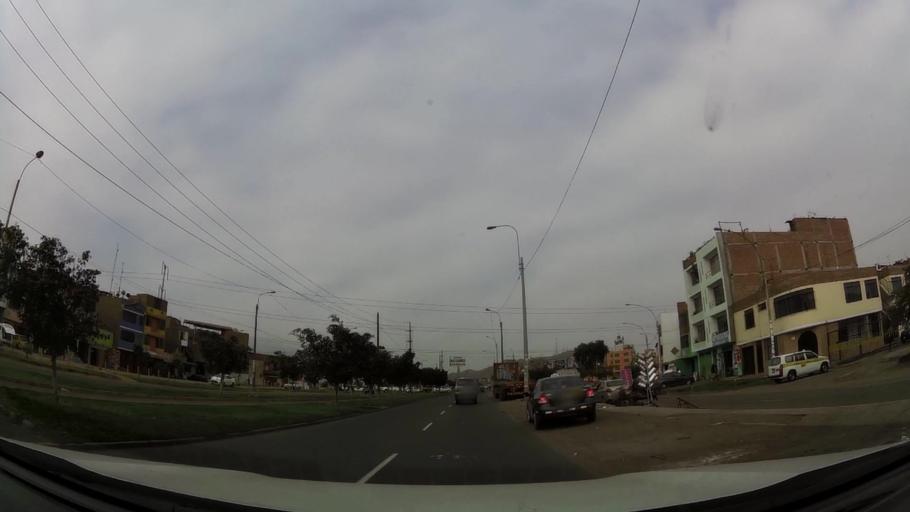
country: PE
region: Lima
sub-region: Lima
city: Independencia
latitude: -12.0123
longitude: -77.0885
